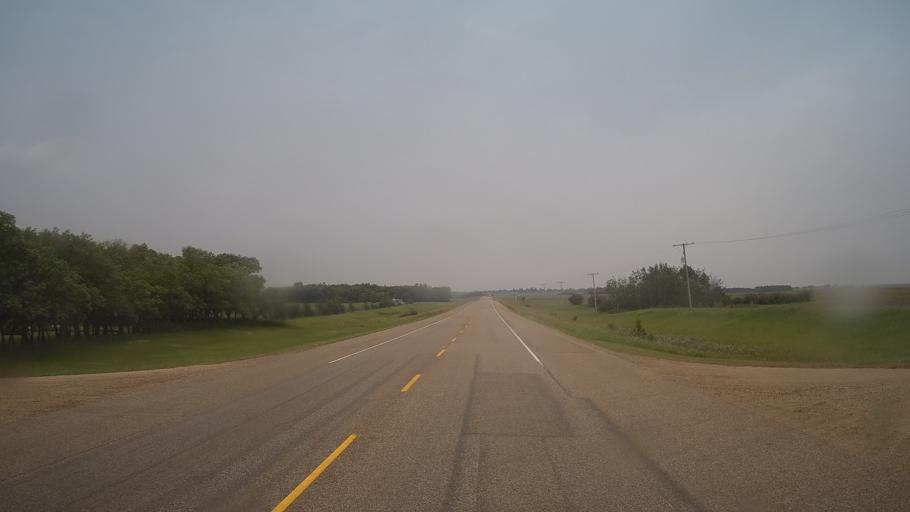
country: CA
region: Saskatchewan
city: Biggar
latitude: 52.0563
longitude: -107.9310
